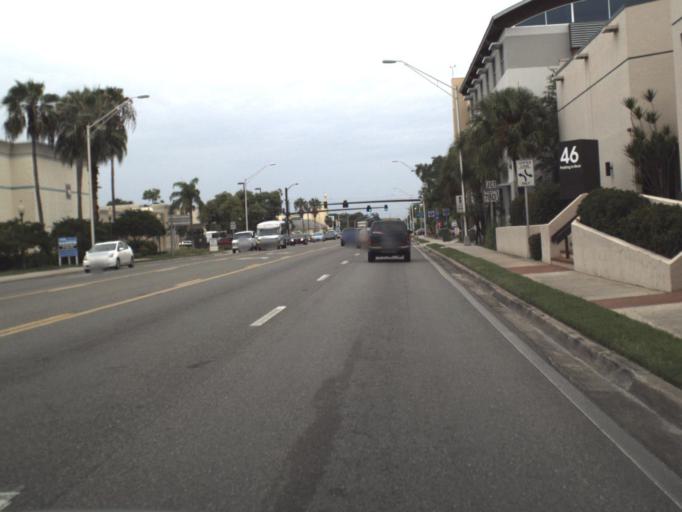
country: US
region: Florida
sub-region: Sarasota County
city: Sarasota
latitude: 27.3371
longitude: -82.5309
